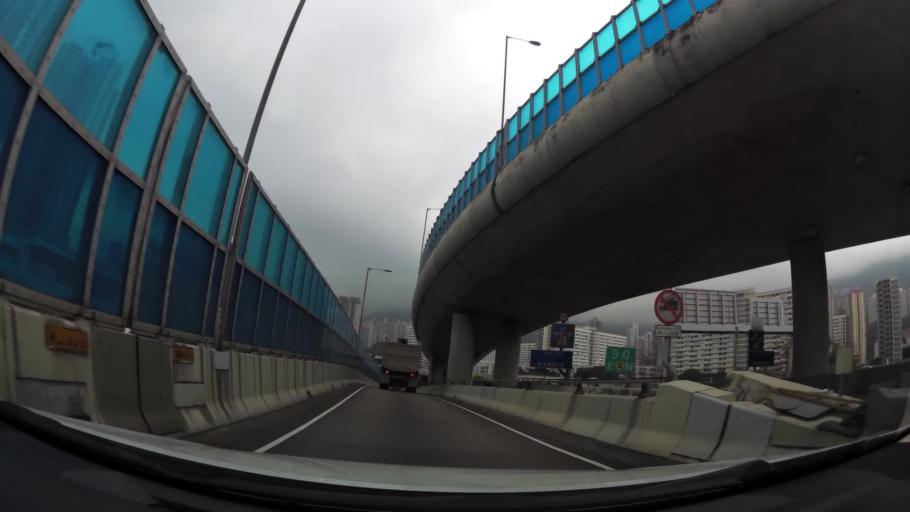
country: HK
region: Kowloon City
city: Kowloon
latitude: 22.3327
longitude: 114.2050
